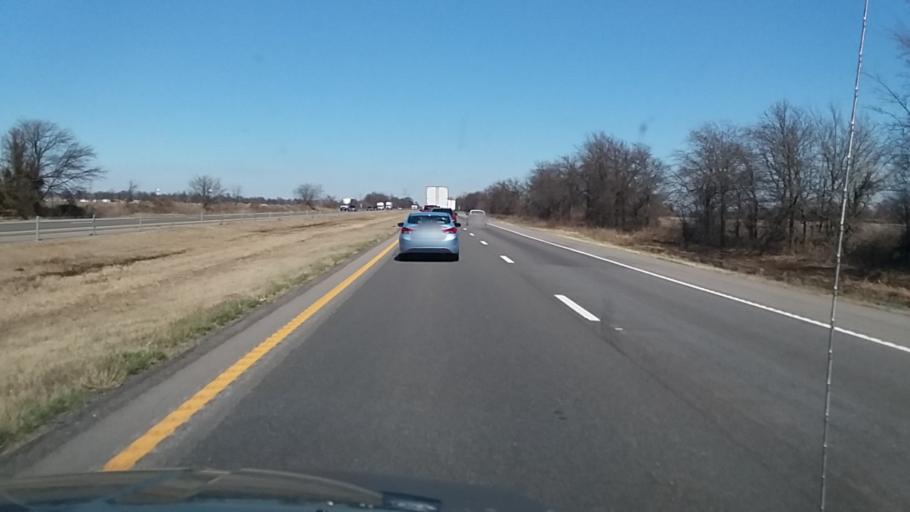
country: US
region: Missouri
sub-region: New Madrid County
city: Lilbourn
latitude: 36.4977
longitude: -89.6181
